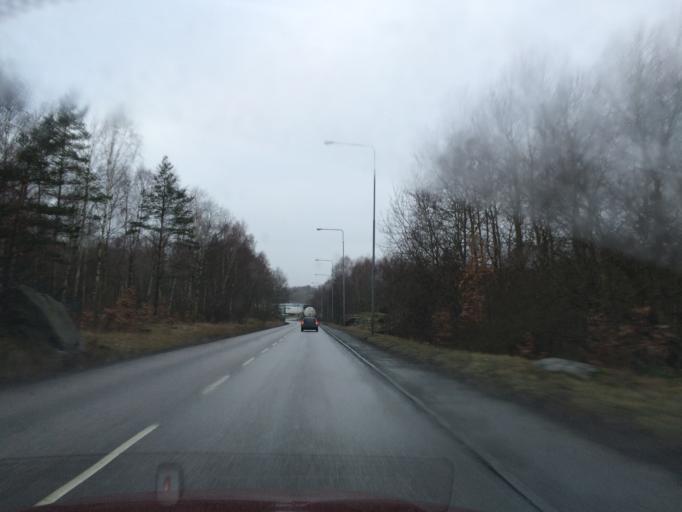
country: SE
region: Vaestra Goetaland
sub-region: Goteborg
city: Majorna
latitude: 57.7048
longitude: 11.8435
